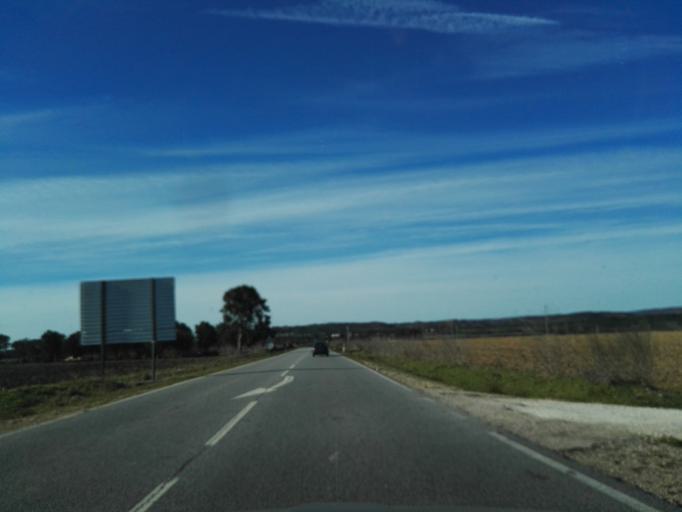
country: PT
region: Santarem
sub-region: Macao
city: Macao
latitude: 39.4655
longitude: -8.0576
